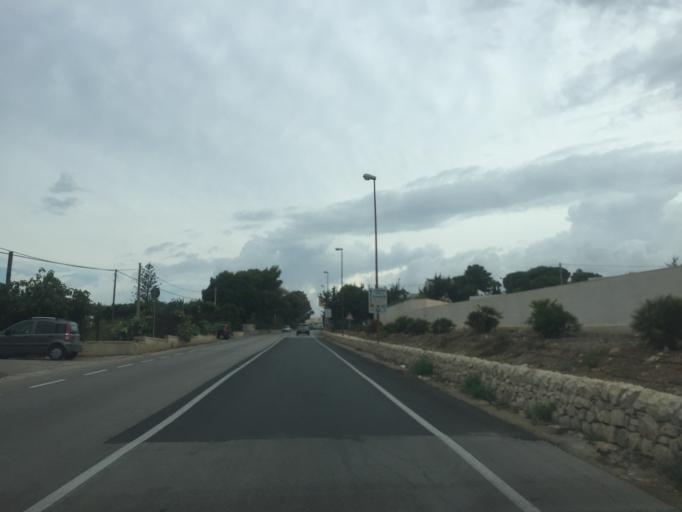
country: IT
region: Sicily
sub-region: Ragusa
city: Marina di Ragusa
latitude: 36.7920
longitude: 14.5521
